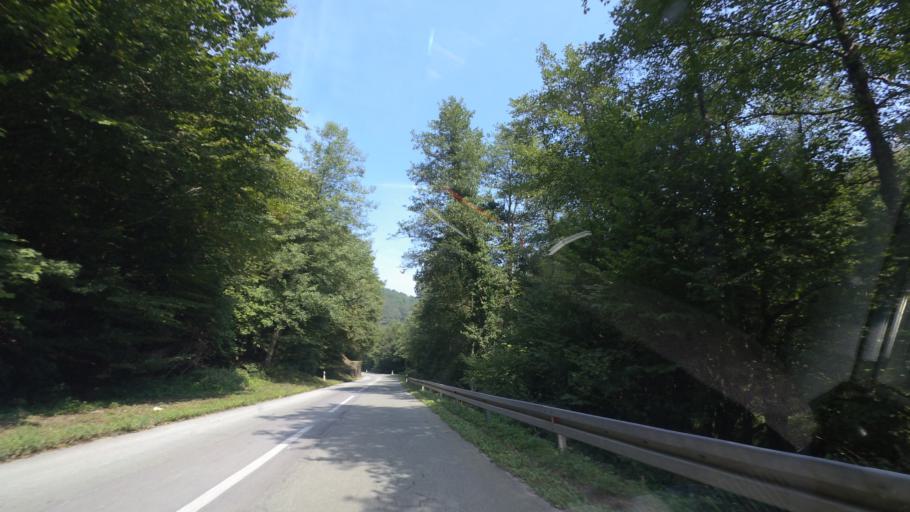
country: HR
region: Sisacko-Moslavacka
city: Glina
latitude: 45.2152
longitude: 16.1309
